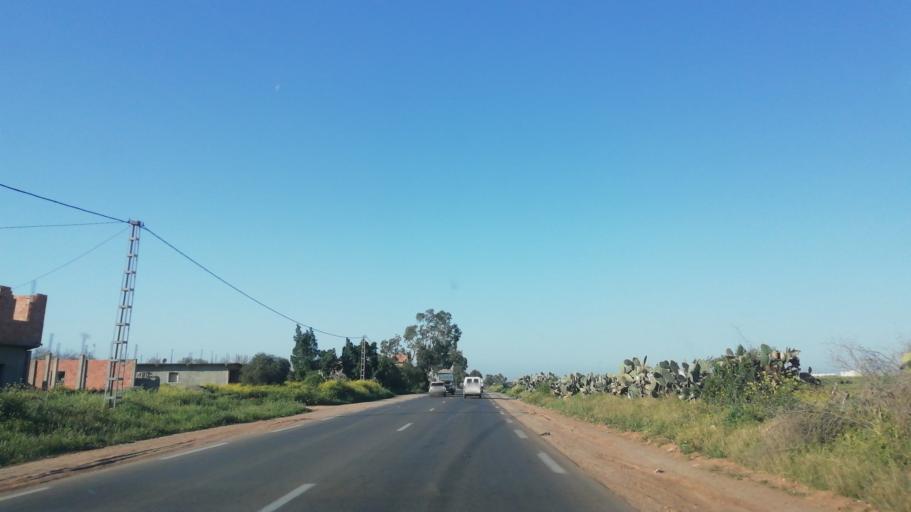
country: DZ
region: Mascara
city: Mascara
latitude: 35.6420
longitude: 0.1549
